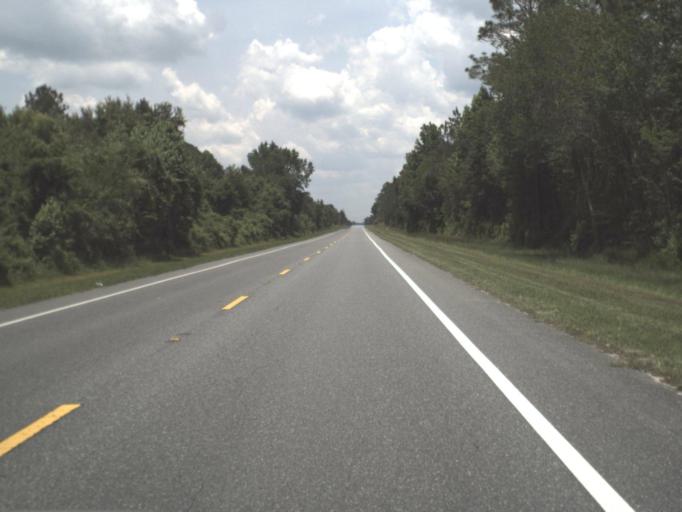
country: US
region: Florida
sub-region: Columbia County
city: Watertown
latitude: 30.1541
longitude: -82.5576
